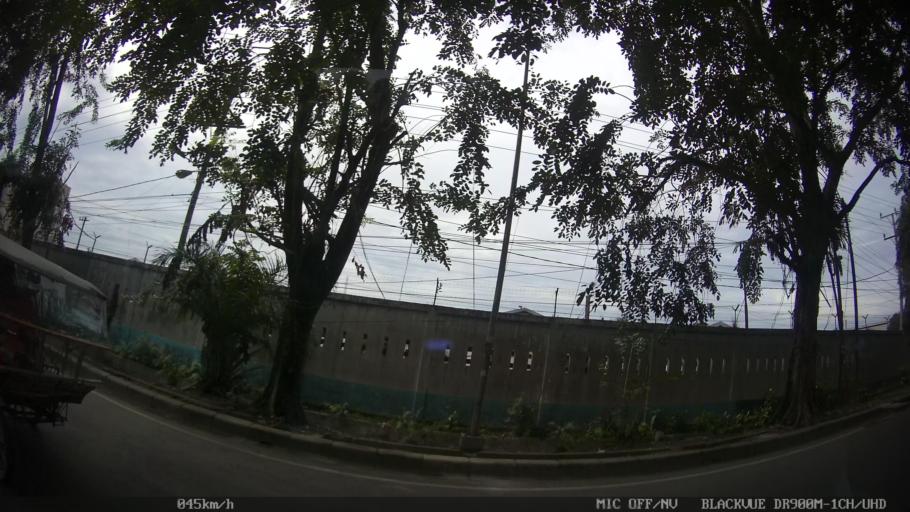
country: ID
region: North Sumatra
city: Sunggal
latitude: 3.5991
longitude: 98.5986
